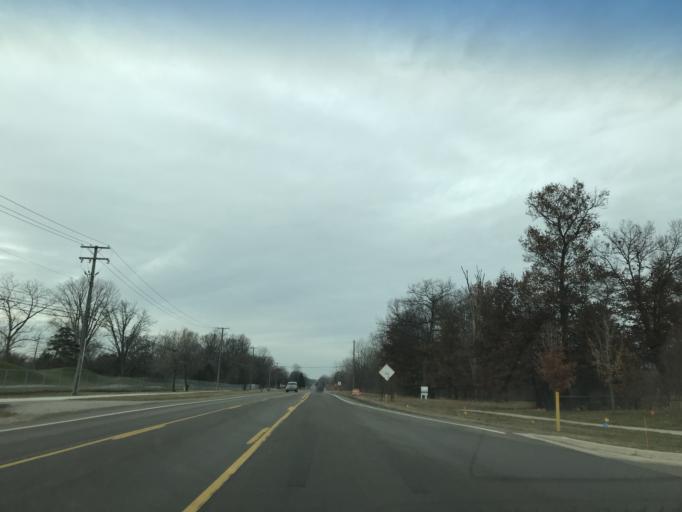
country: US
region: Michigan
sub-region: Oakland County
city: Troy
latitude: 42.6240
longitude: -83.1005
